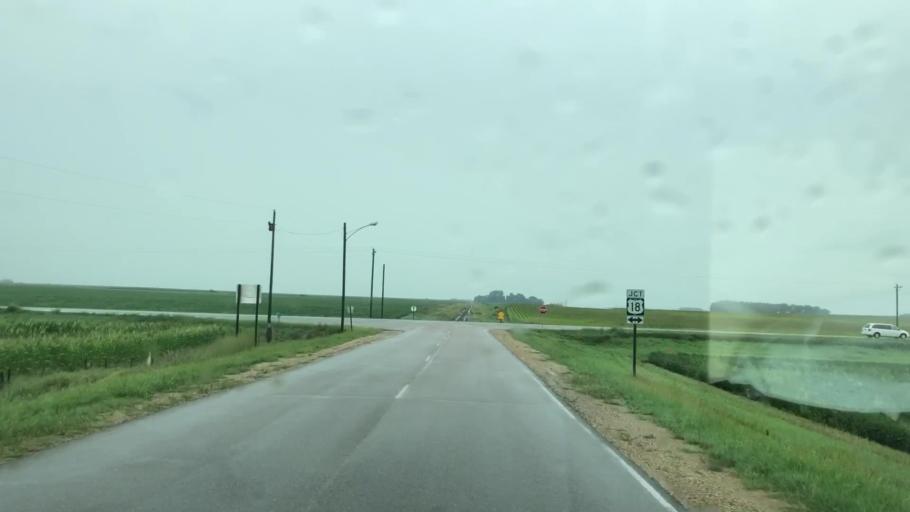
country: US
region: Iowa
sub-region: O'Brien County
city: Sanborn
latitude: 43.1872
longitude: -95.7230
